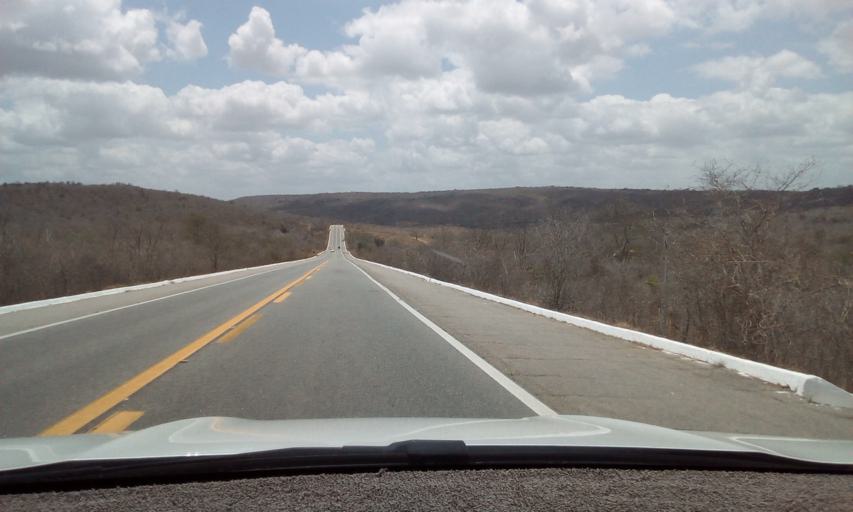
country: BR
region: Paraiba
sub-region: Boqueirao
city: Boqueirao
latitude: -7.6767
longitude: -36.0713
